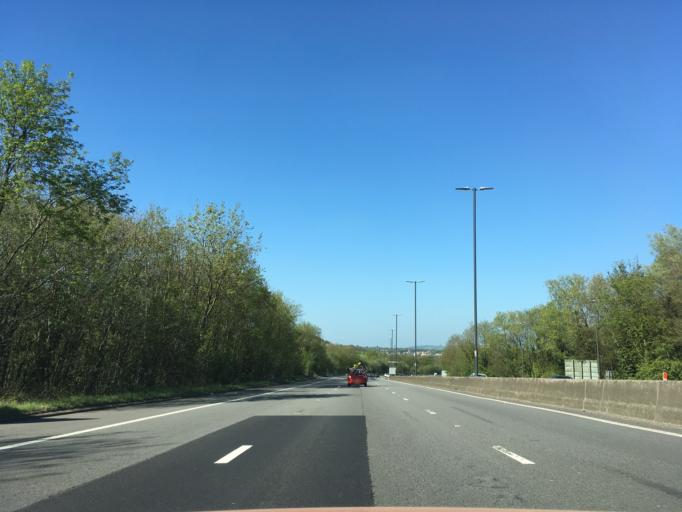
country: GB
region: Wales
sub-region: Newport
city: Newport
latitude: 51.5889
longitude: -3.0321
